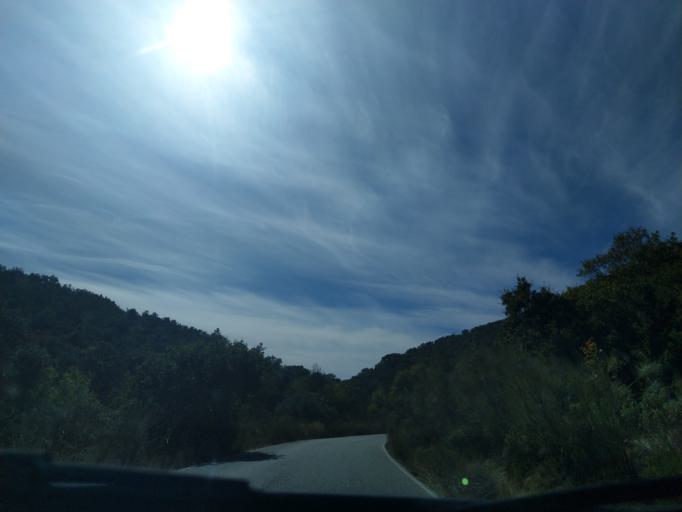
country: ES
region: Extremadura
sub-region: Provincia de Badajoz
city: Reina
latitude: 38.1219
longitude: -5.9133
